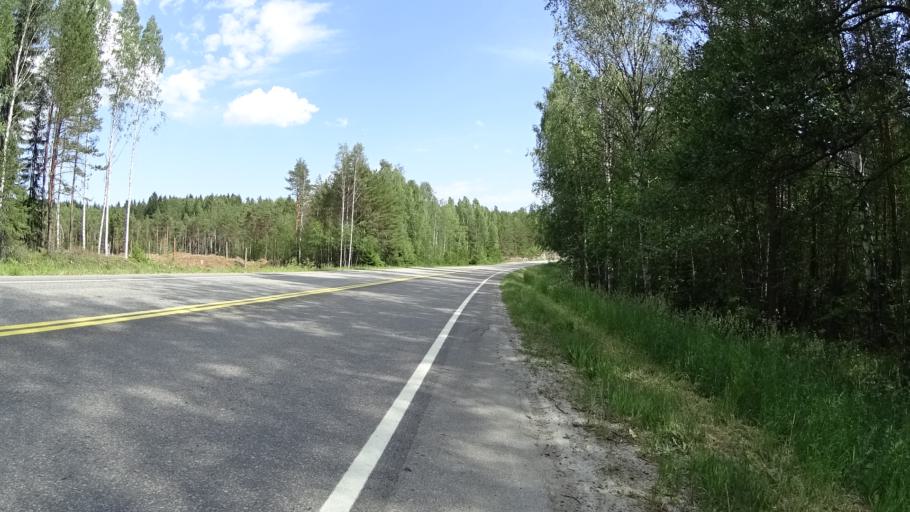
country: FI
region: Uusimaa
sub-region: Raaseporin
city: Pohja
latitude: 60.1025
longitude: 23.5740
